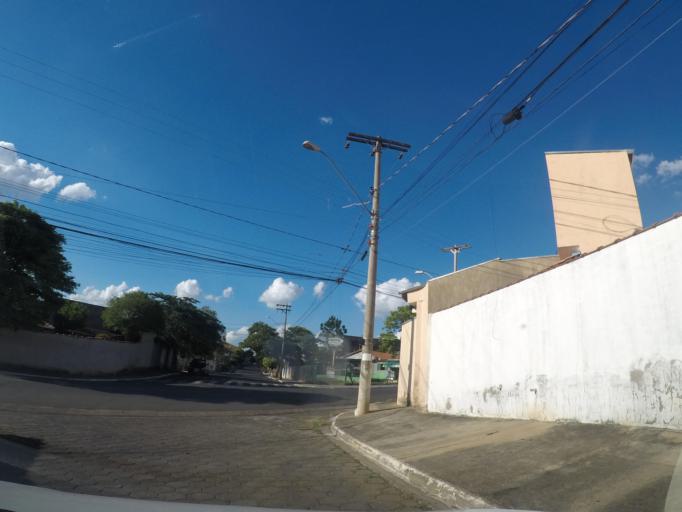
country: BR
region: Sao Paulo
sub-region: Sumare
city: Sumare
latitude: -22.8092
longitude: -47.2222
